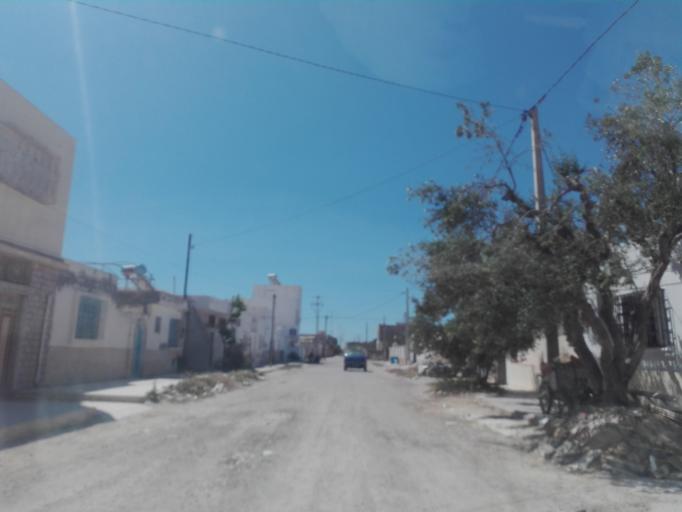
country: TN
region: Safaqis
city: Jabinyanah
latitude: 34.7428
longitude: 11.2975
